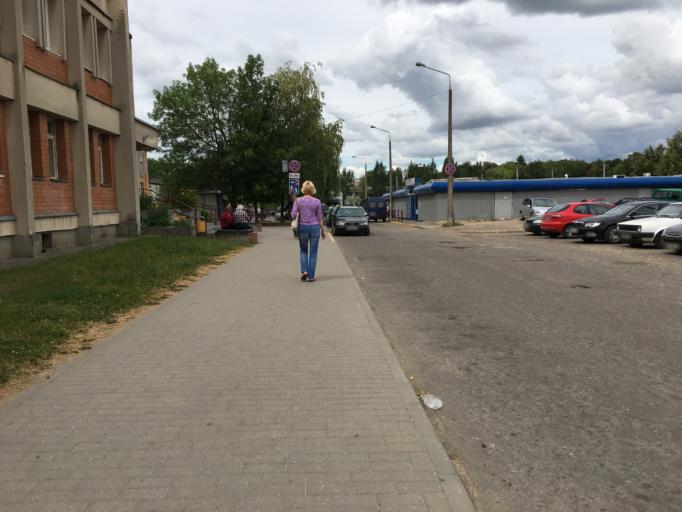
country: BY
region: Grodnenskaya
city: Hrodna
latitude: 53.7057
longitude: 23.8423
